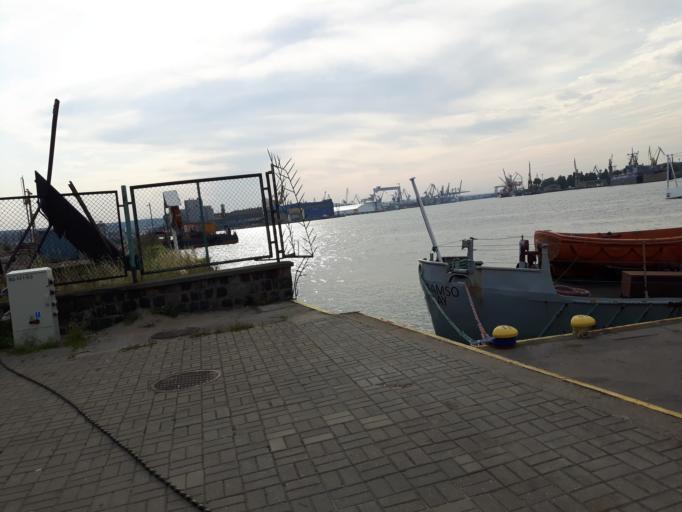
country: PL
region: Pomeranian Voivodeship
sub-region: Gdynia
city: Gdynia
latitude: 54.5341
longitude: 18.5478
